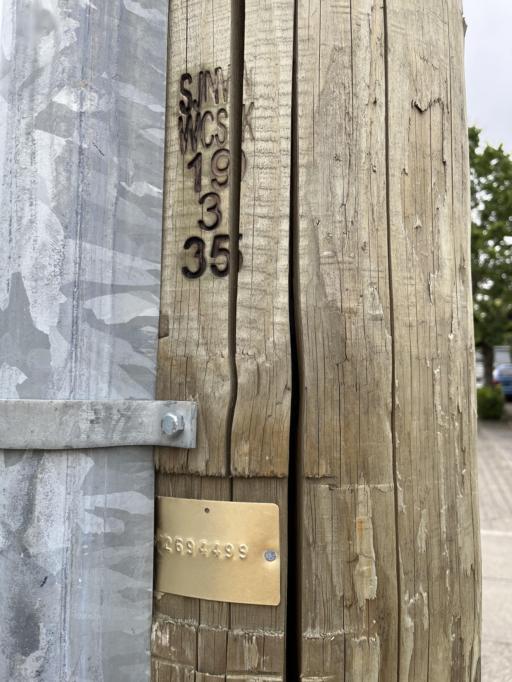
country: CA
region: British Columbia
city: Ladner
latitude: 49.0908
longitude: -123.0829
